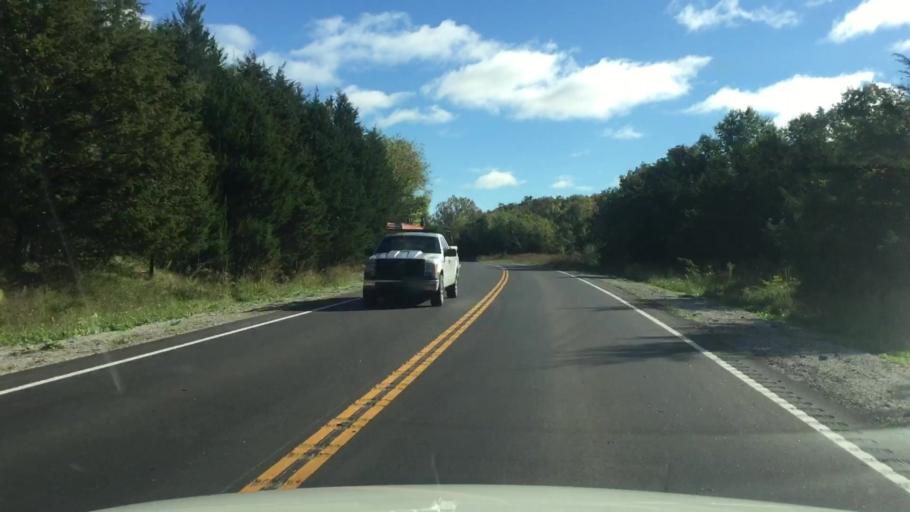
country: US
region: Missouri
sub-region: Howard County
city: New Franklin
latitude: 38.9846
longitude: -92.5438
